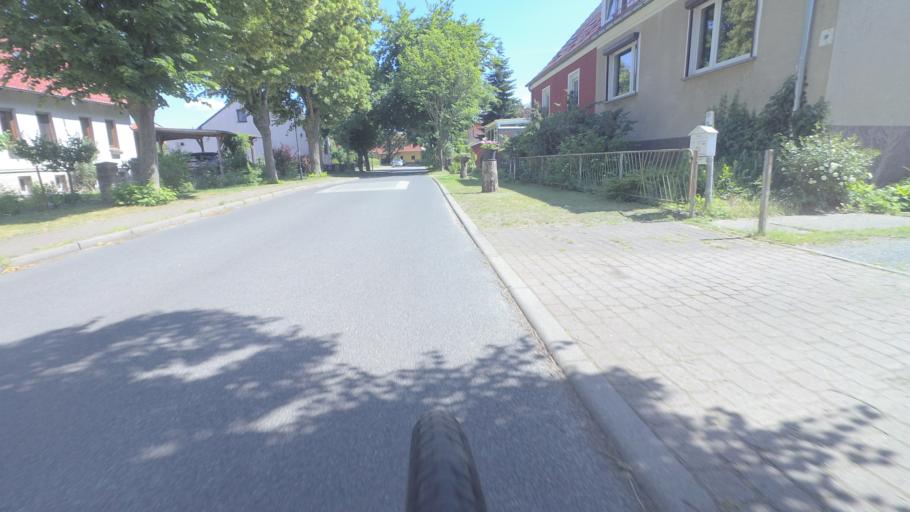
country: DE
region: Brandenburg
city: Rangsdorf
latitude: 52.2678
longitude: 13.4643
